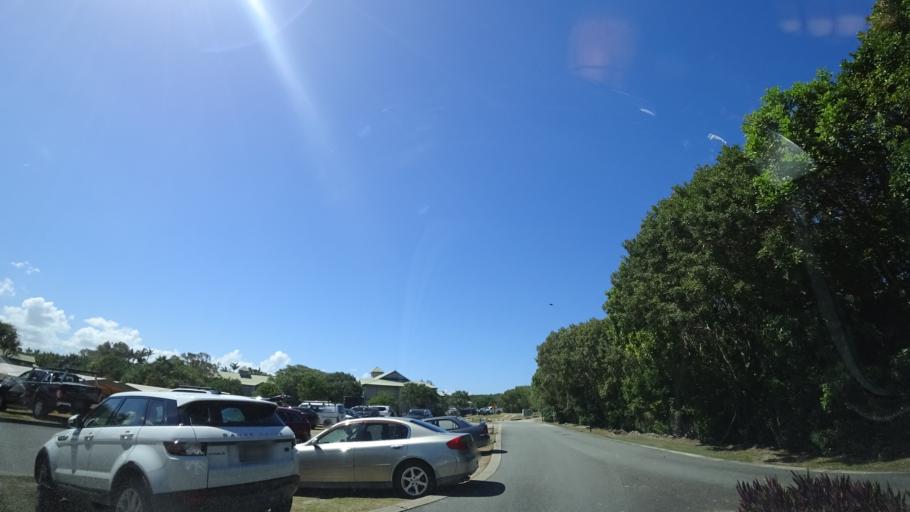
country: AU
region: Queensland
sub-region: Sunshine Coast
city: Mooloolaba
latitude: -26.6330
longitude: 153.1001
